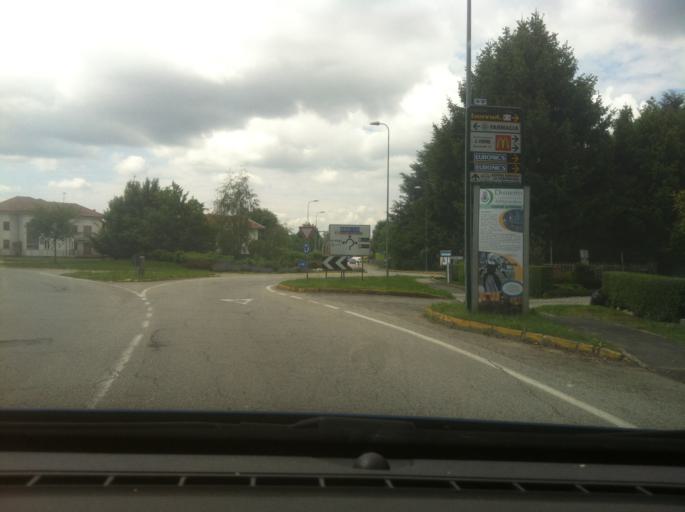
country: IT
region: Piedmont
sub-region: Provincia di Torino
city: Pavone Canavese
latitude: 45.4445
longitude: 7.8557
